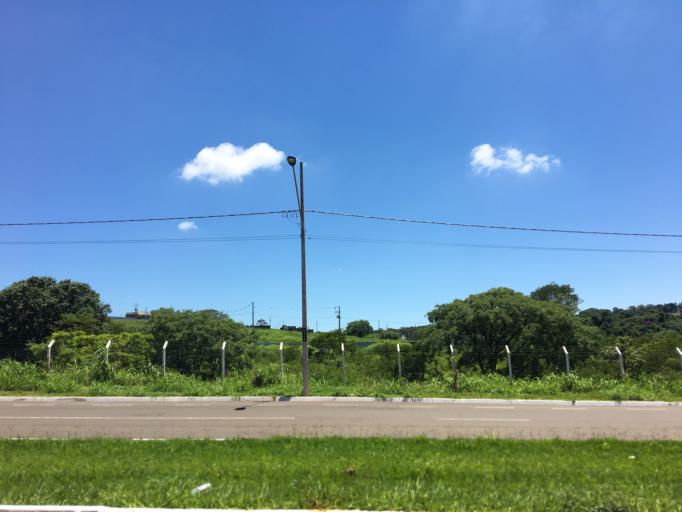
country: BR
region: Parana
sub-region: Maringa
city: Maringa
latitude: -23.4494
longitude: -51.9735
